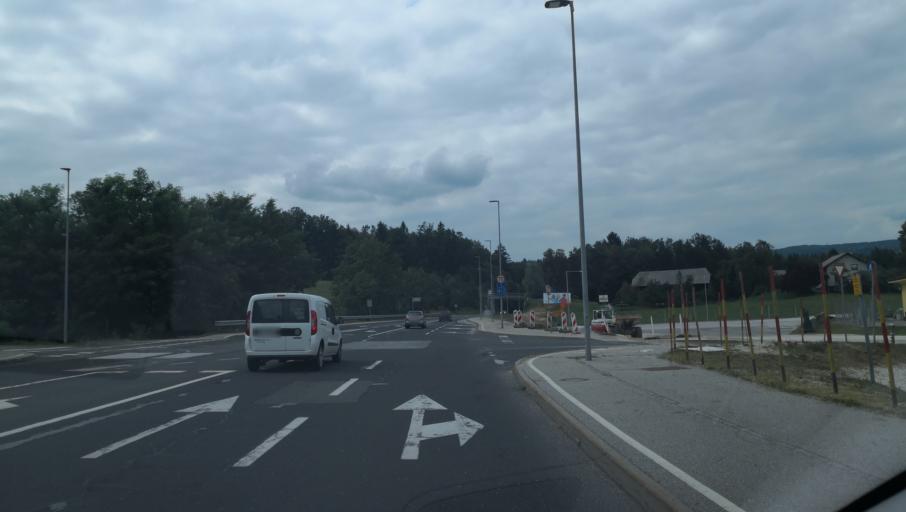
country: SI
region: Novo Mesto
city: Novo Mesto
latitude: 45.8175
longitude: 15.1721
